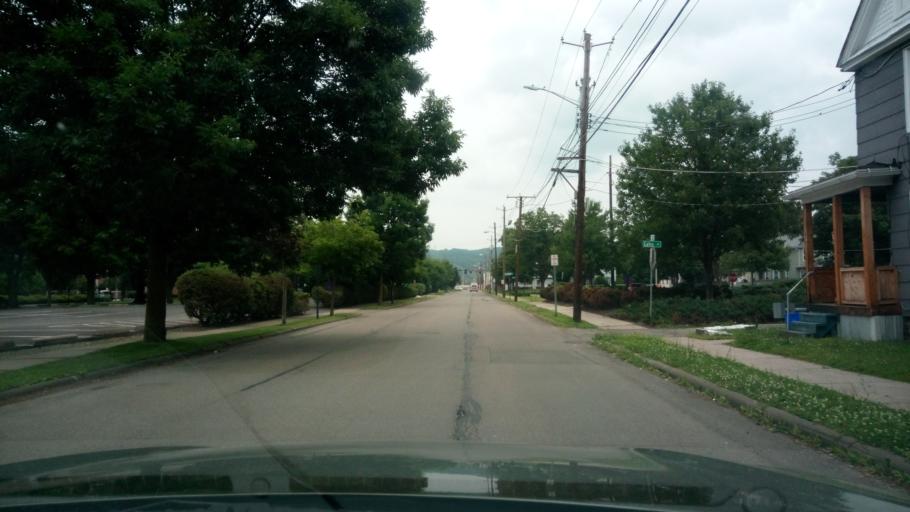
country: US
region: New York
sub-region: Chemung County
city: Elmira
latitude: 42.0950
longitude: -76.8148
